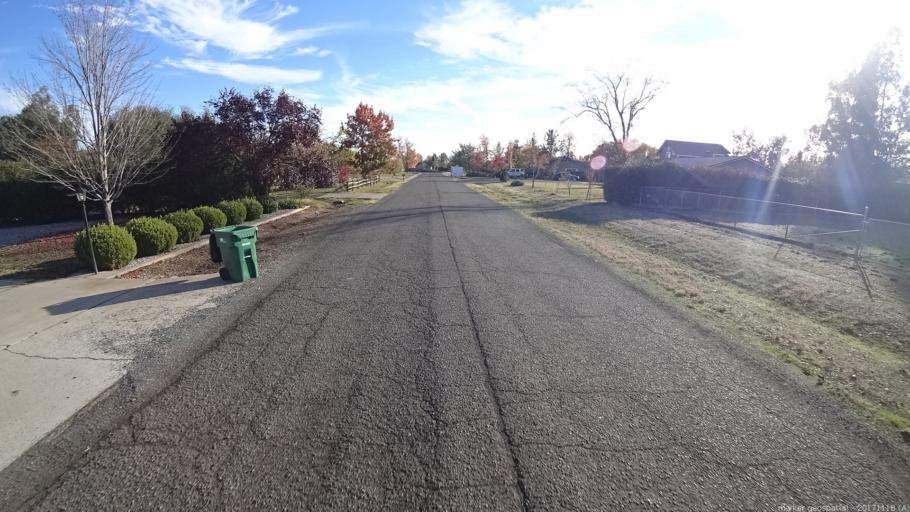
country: US
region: California
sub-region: Shasta County
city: Cottonwood
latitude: 40.3827
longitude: -122.3366
